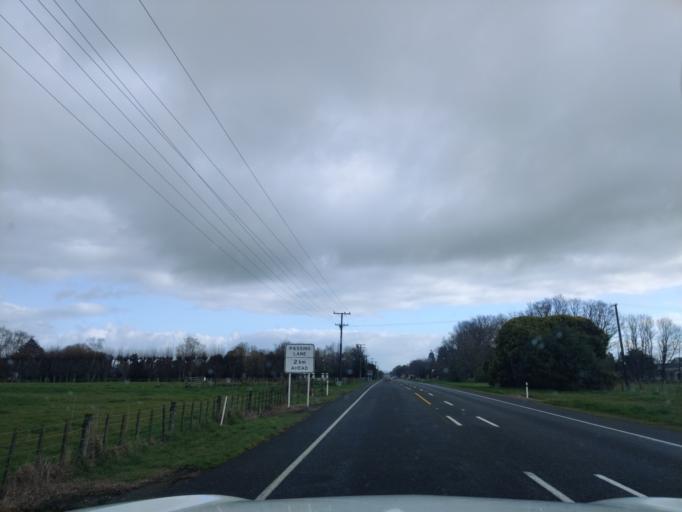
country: NZ
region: Manawatu-Wanganui
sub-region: Palmerston North City
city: Palmerston North
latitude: -40.3291
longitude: 175.5861
